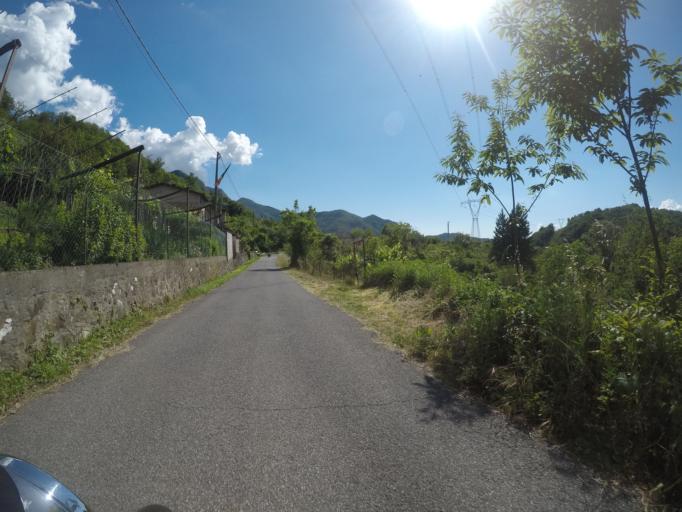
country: IT
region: Tuscany
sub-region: Provincia di Massa-Carrara
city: Casola in Lunigiana
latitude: 44.1757
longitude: 10.1495
